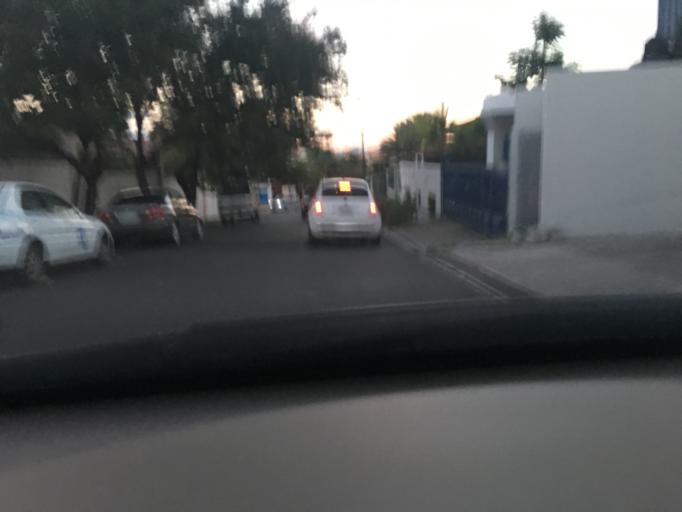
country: DO
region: Nacional
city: Santo Domingo
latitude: 18.4888
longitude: -69.9631
